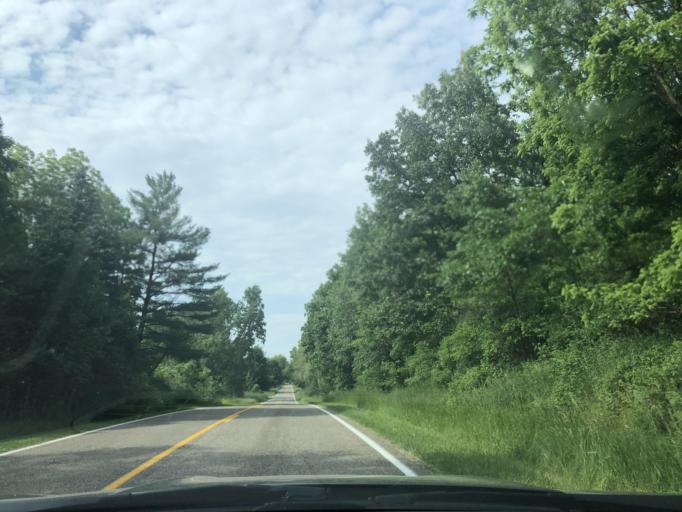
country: US
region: Michigan
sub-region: Clinton County
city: Bath
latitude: 42.8836
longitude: -84.4780
